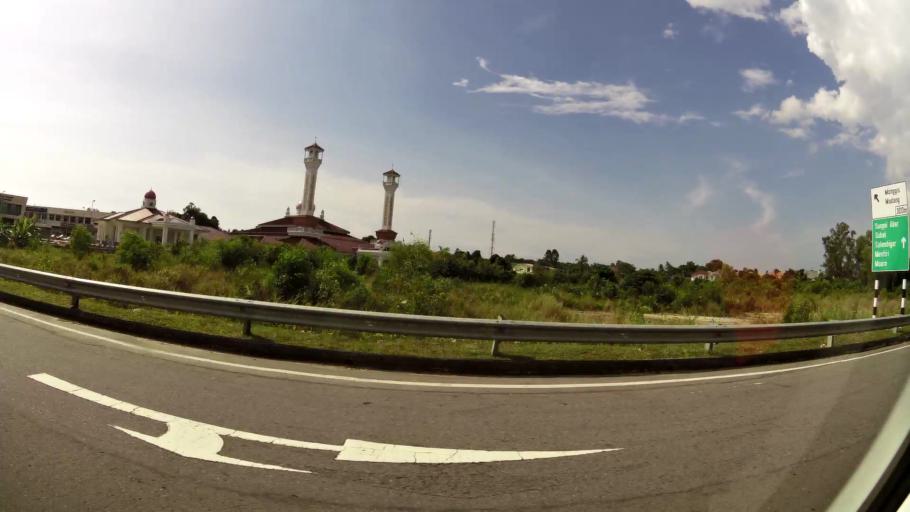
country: BN
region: Brunei and Muara
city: Bandar Seri Begawan
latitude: 4.9531
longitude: 114.9559
